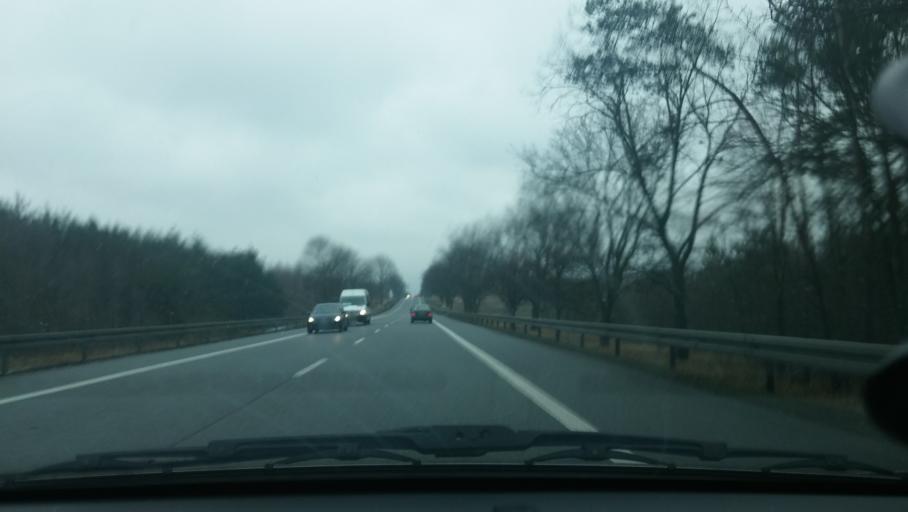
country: PL
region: Masovian Voivodeship
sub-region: Powiat wegrowski
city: Grebkow
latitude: 52.2054
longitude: 21.9377
